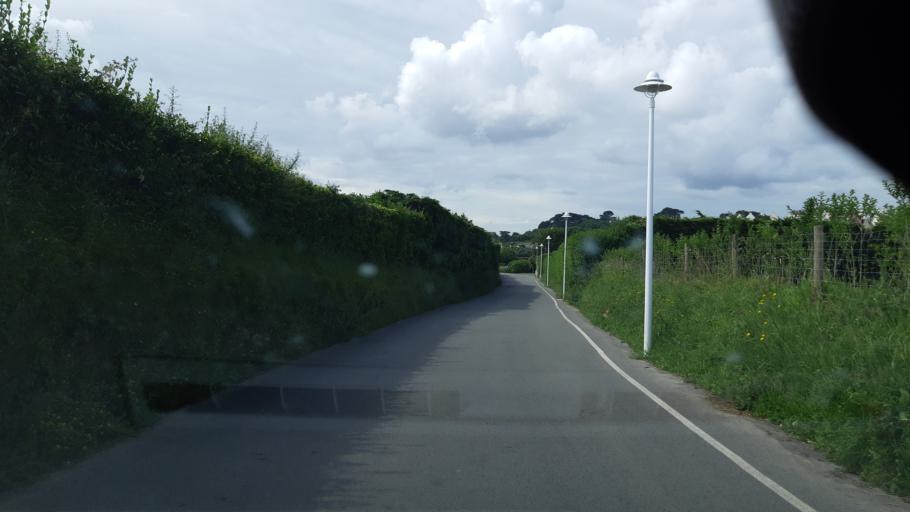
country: FR
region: Brittany
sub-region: Departement du Finistere
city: Saint-Pol-de-Leon
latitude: 48.6922
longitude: -3.9676
